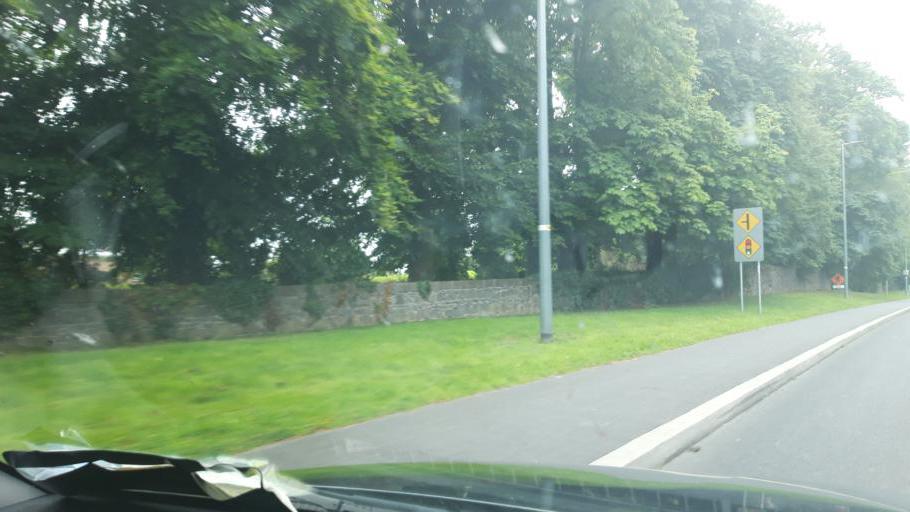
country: IE
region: Leinster
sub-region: Kilkenny
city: Kilkenny
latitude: 52.6393
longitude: -7.2685
